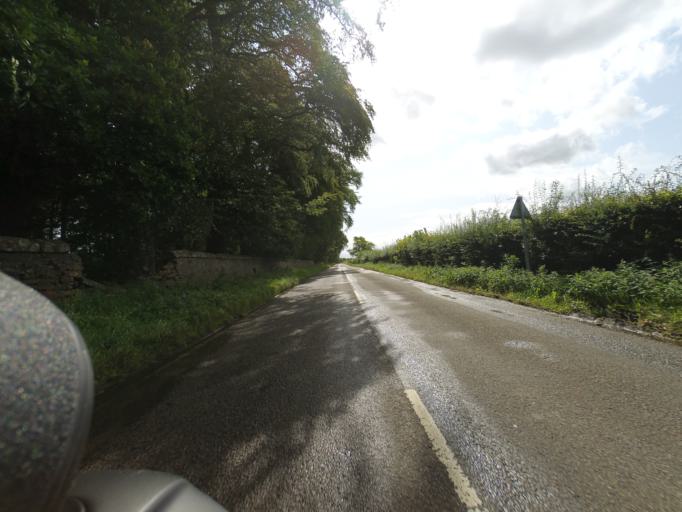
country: GB
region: Scotland
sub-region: Highland
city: Tain
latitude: 57.7383
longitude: -4.0809
